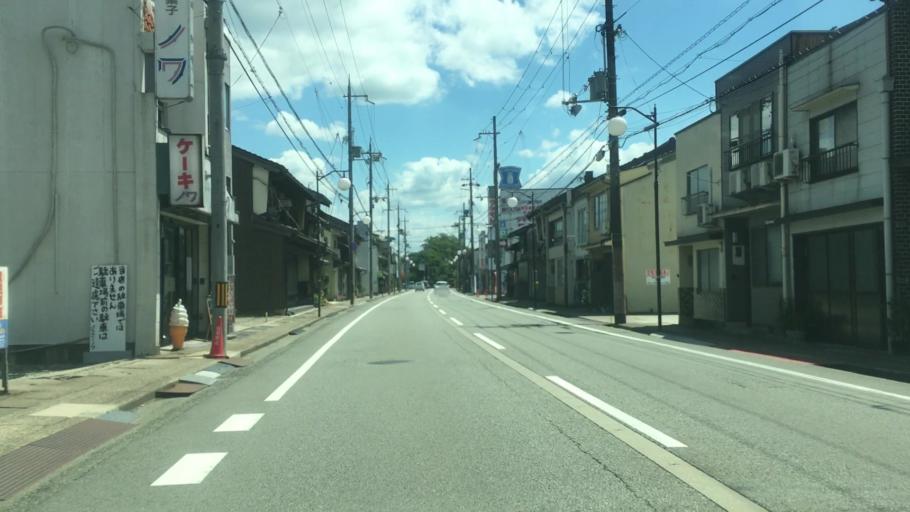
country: JP
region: Hyogo
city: Toyooka
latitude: 35.5373
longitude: 134.8250
